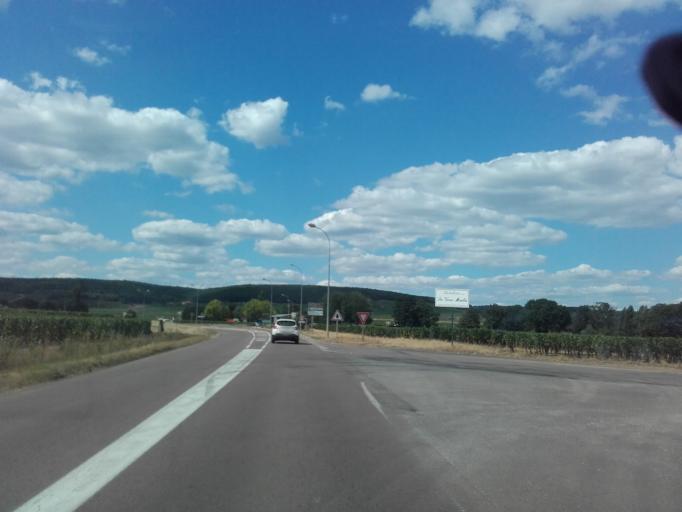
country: FR
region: Bourgogne
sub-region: Departement de la Cote-d'Or
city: Beaune
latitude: 47.0517
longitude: 4.8393
